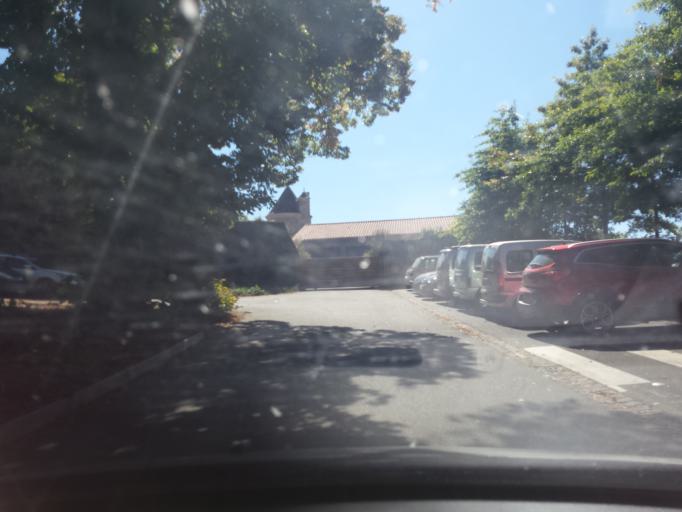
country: FR
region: Pays de la Loire
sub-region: Departement de la Vendee
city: Apremont
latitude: 46.7500
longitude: -1.7417
